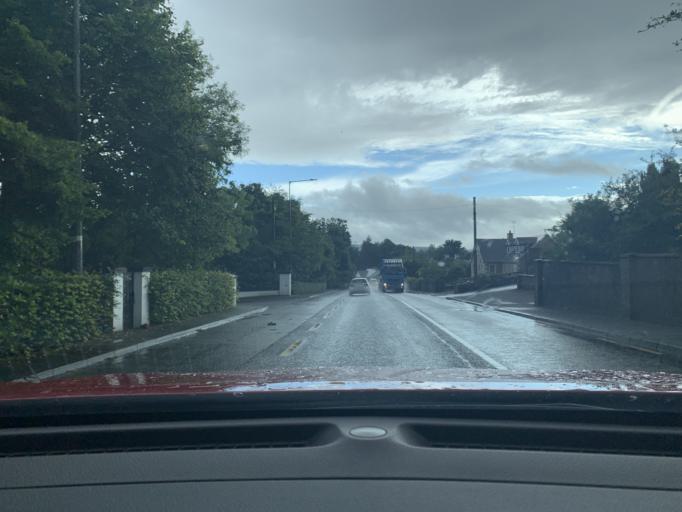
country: IE
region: Ulster
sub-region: County Donegal
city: Ballybofey
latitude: 54.8092
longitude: -7.7659
